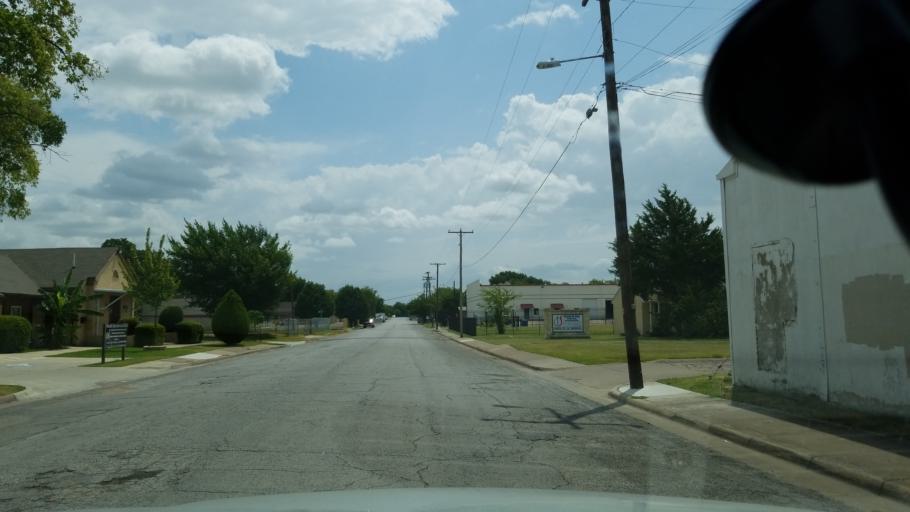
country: US
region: Texas
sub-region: Dallas County
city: Grand Prairie
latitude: 32.7525
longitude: -96.9771
